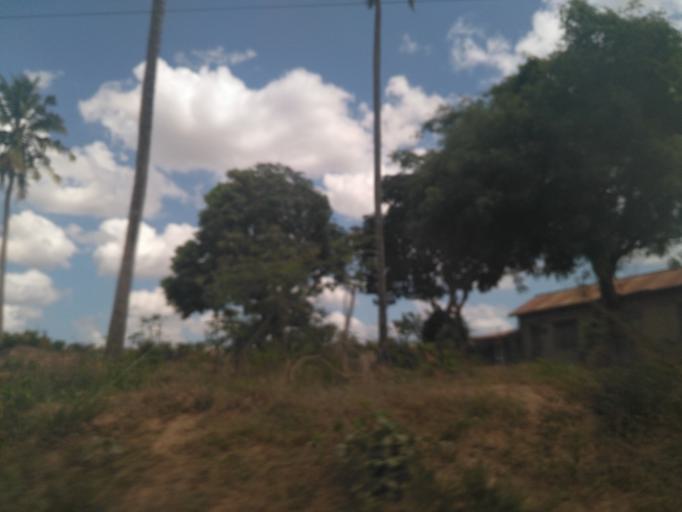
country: TZ
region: Dar es Salaam
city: Dar es Salaam
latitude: -6.9063
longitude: 39.2371
